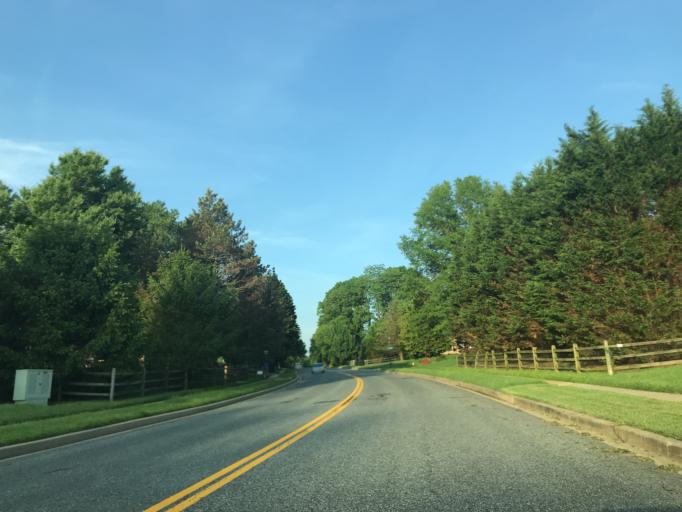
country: US
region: Maryland
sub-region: Harford County
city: North Bel Air
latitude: 39.5569
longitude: -76.3425
